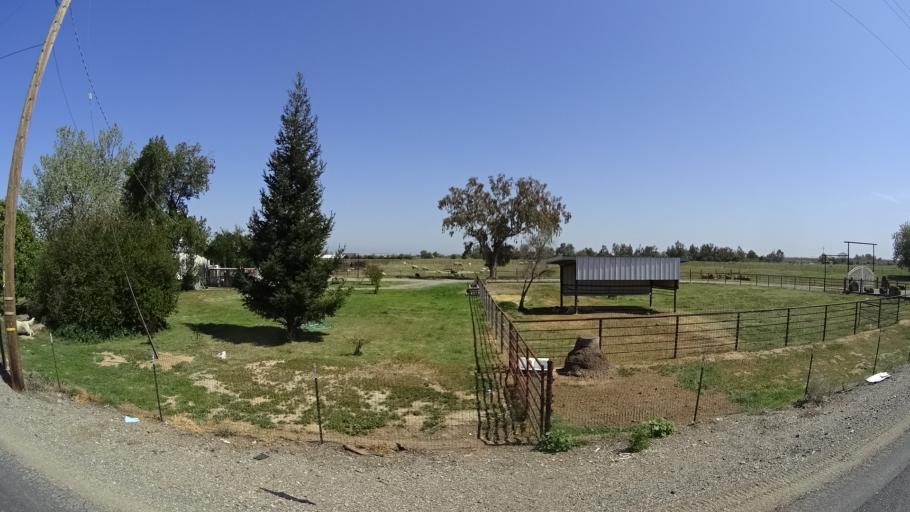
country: US
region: California
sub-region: Glenn County
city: Orland
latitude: 39.7728
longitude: -122.1968
